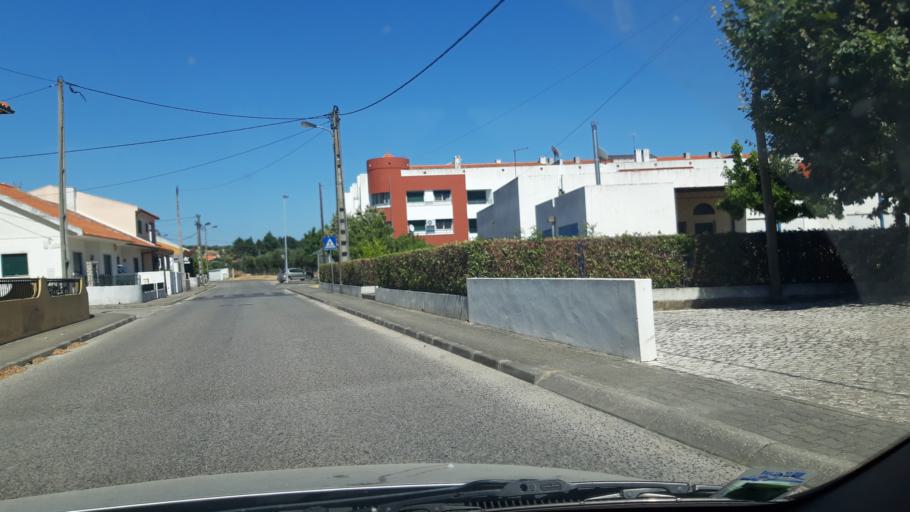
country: PT
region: Santarem
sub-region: Entroncamento
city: Entroncamento
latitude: 39.4650
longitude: -8.4536
